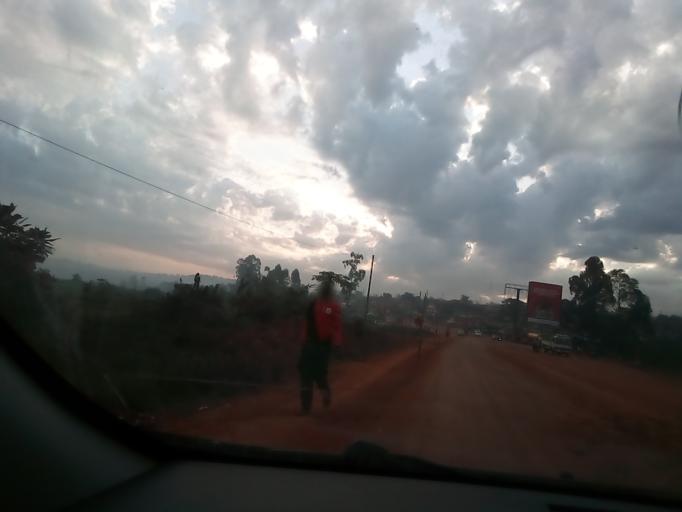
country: UG
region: Central Region
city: Masaka
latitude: -0.3281
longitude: 31.7498
